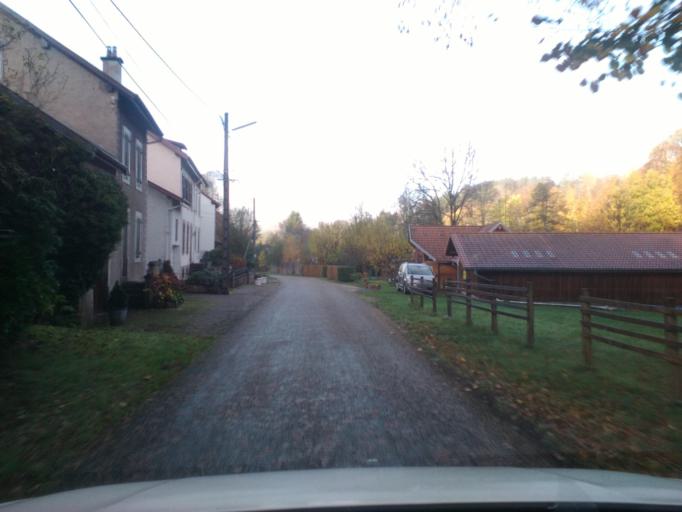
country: FR
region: Lorraine
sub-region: Departement des Vosges
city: Senones
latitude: 48.4180
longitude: 7.0599
